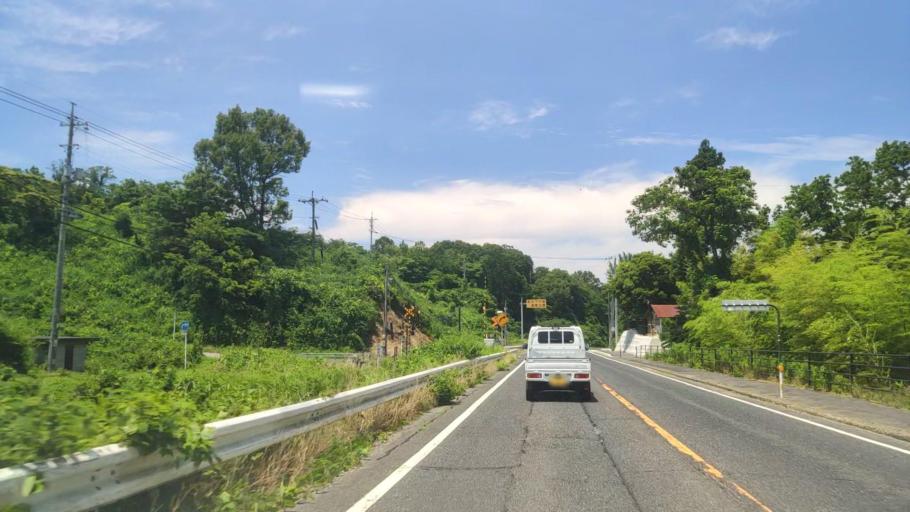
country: JP
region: Tottori
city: Tottori
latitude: 35.4331
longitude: 134.2580
